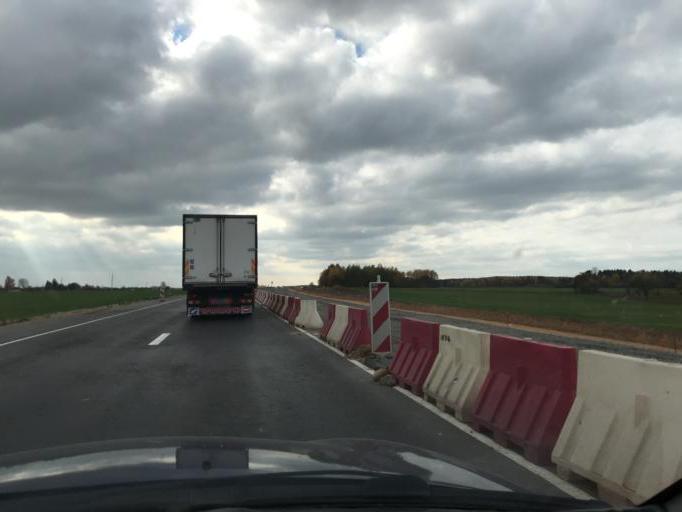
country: BY
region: Grodnenskaya
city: Lida
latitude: 53.8145
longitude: 25.1167
